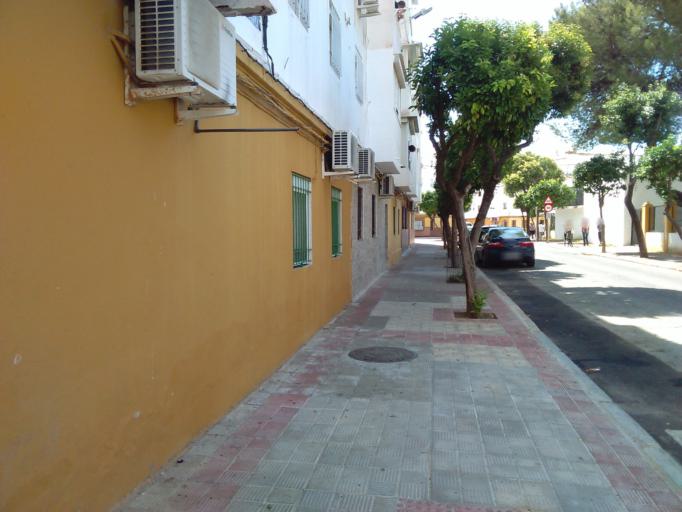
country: ES
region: Andalusia
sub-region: Provincia de Sevilla
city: La Algaba
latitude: 37.4282
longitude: -5.9835
